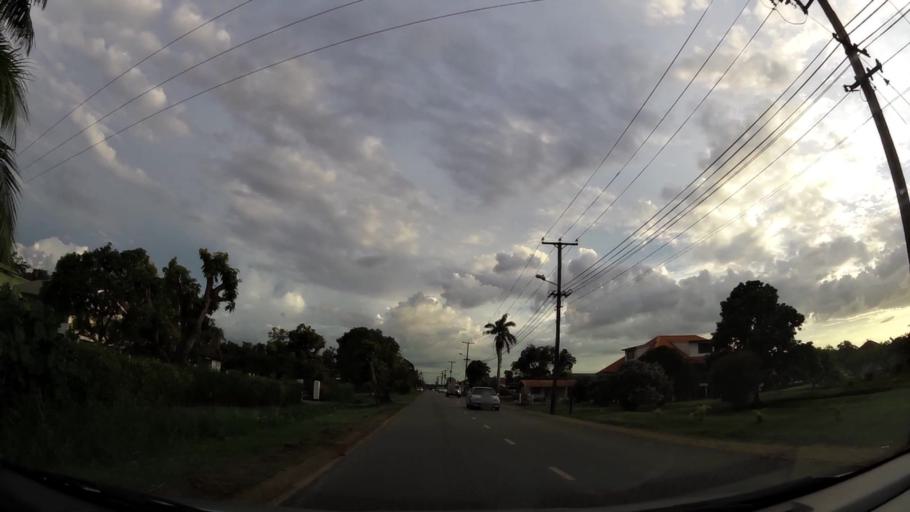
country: SR
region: Paramaribo
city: Paramaribo
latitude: 5.7840
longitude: -55.1655
